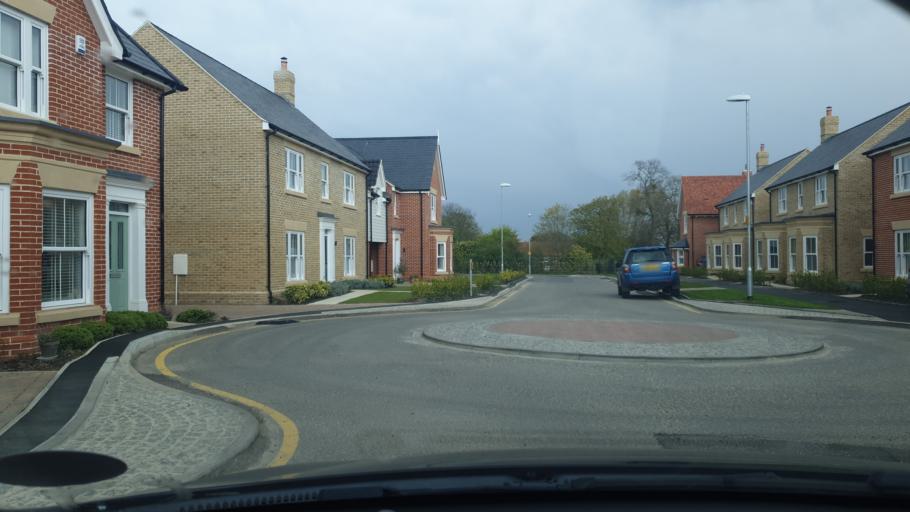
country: GB
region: England
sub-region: Essex
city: Manningtree
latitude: 51.9415
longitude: 1.0498
